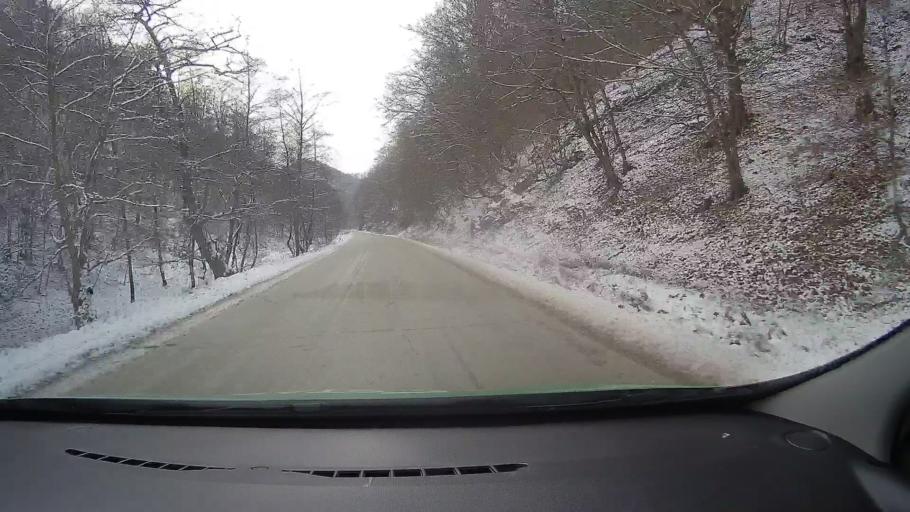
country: RO
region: Alba
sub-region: Oras Zlatna
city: Zlatna
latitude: 46.1059
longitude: 23.1936
